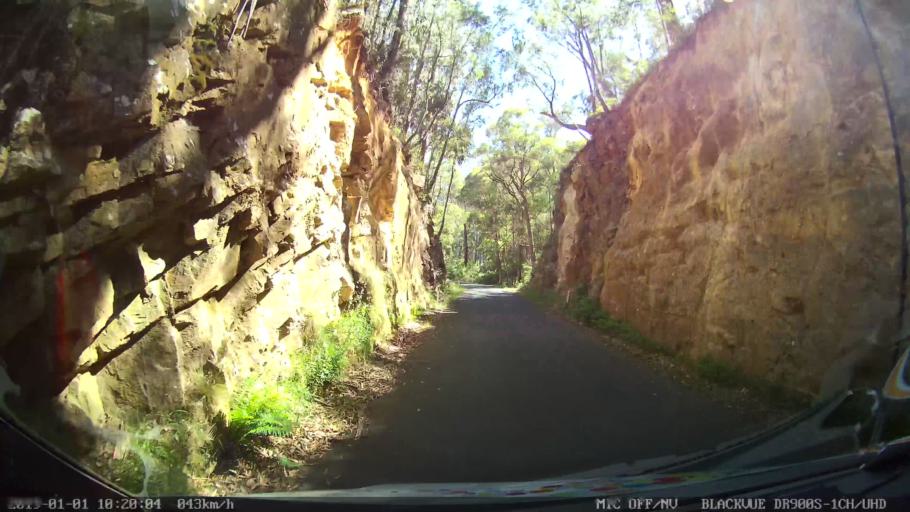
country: AU
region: New South Wales
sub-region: Snowy River
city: Jindabyne
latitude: -36.0806
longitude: 148.1871
